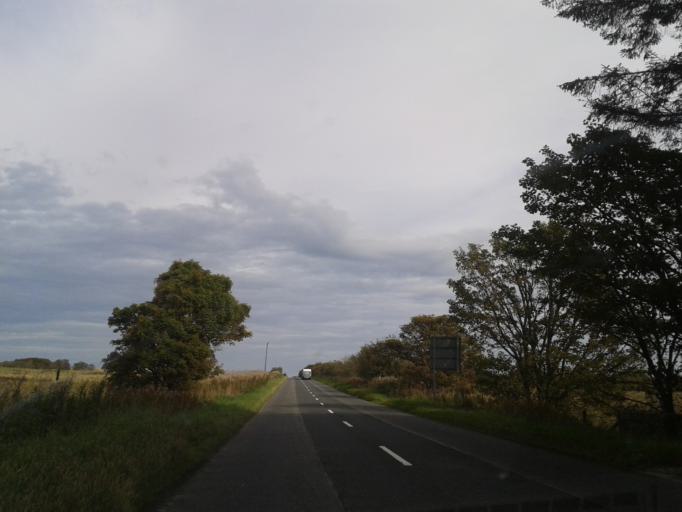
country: GB
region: Scotland
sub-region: Aberdeenshire
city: Turriff
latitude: 57.5941
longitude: -2.3005
